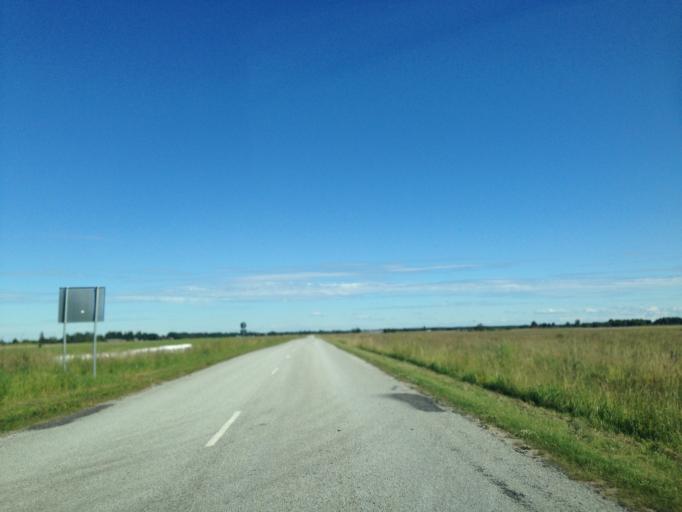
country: EE
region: Harju
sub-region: Kuusalu vald
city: Kuusalu
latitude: 59.4674
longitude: 25.3158
